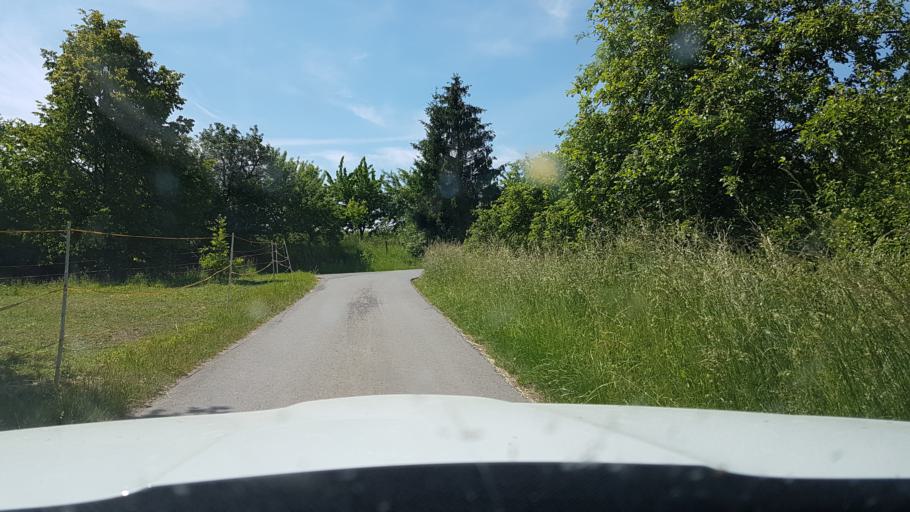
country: DE
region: Bavaria
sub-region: Regierungsbezirk Unterfranken
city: Wonfurt
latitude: 49.9961
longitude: 10.4961
